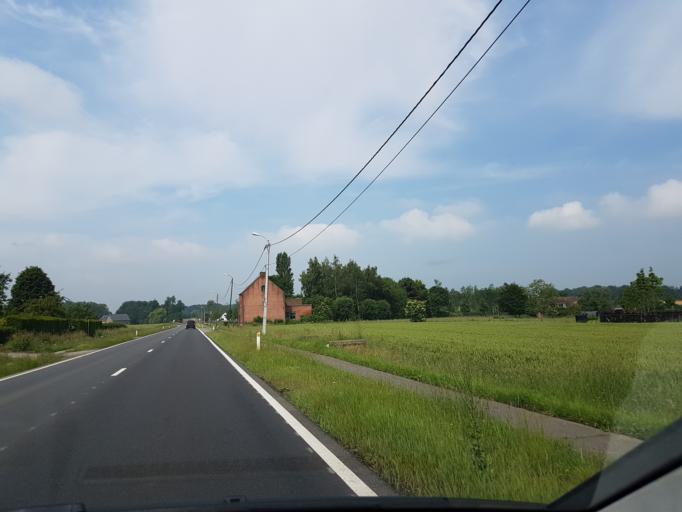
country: BE
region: Flanders
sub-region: Provincie Vlaams-Brabant
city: Meise
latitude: 50.9517
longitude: 4.2861
